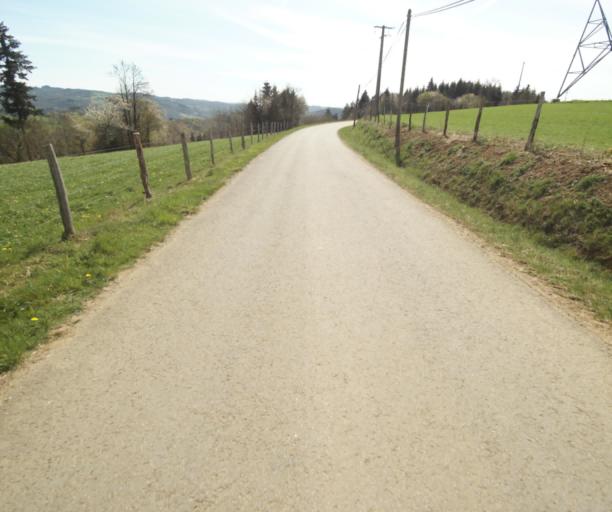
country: FR
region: Limousin
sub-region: Departement de la Correze
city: Naves
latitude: 45.3662
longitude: 1.8029
